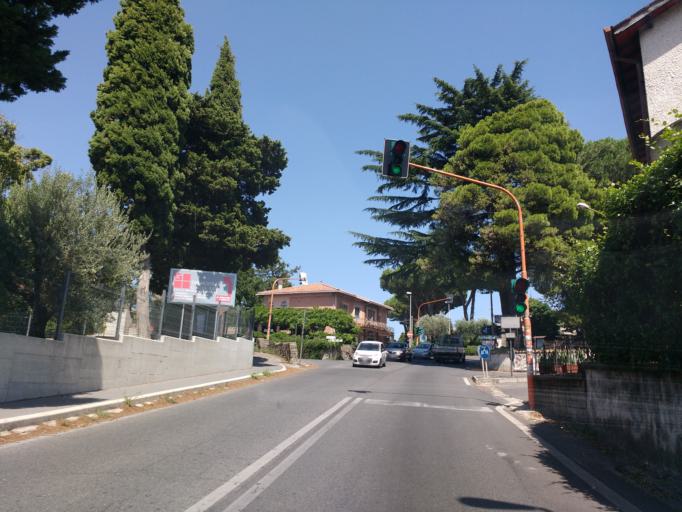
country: IT
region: Latium
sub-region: Citta metropolitana di Roma Capitale
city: Rocca di Papa
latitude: 41.7744
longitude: 12.6960
